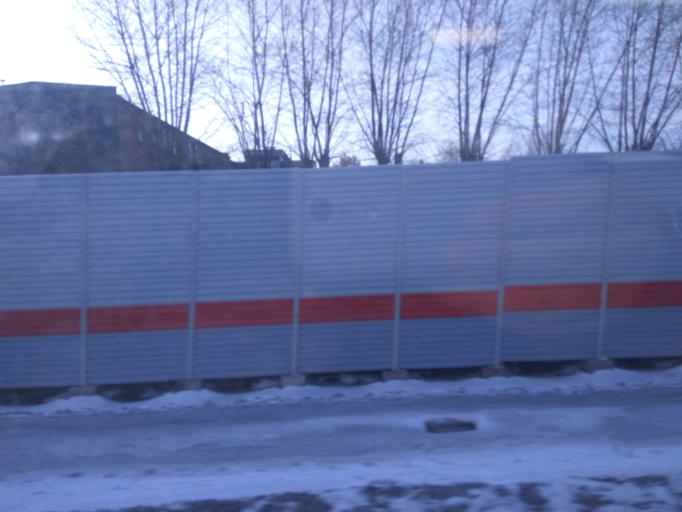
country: RU
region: Moskovskaya
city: Bogorodskoye
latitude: 55.8197
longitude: 37.7305
